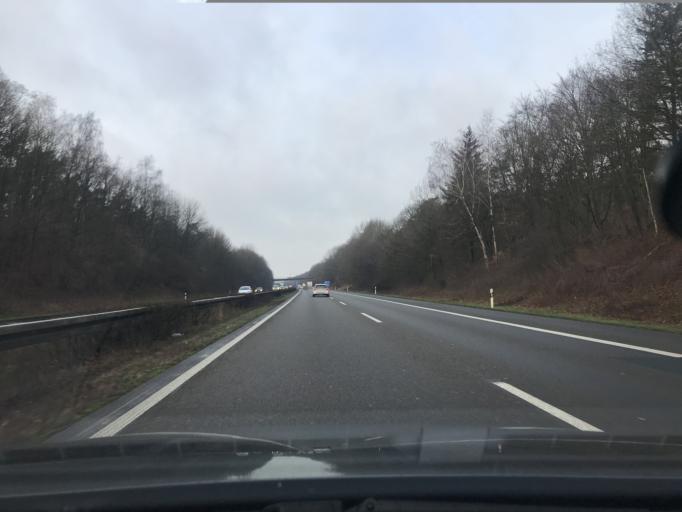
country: DE
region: North Rhine-Westphalia
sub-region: Regierungsbezirk Dusseldorf
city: Alpen
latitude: 51.5619
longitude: 6.5112
